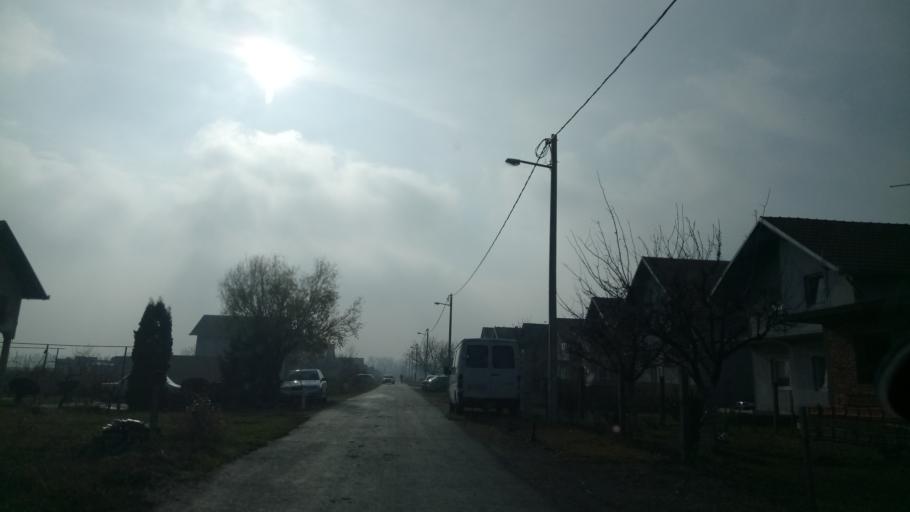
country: RS
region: Autonomna Pokrajina Vojvodina
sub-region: Sremski Okrug
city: Stara Pazova
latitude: 44.9809
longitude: 20.1749
